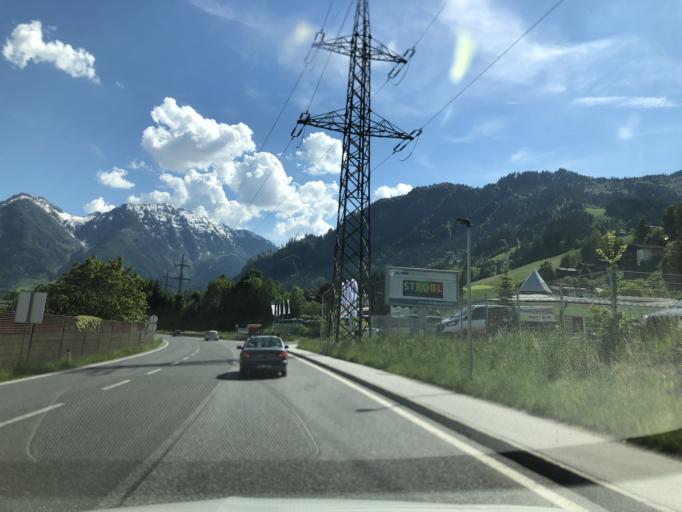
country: AT
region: Salzburg
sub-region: Politischer Bezirk Sankt Johann im Pongau
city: Sankt Johann im Pongau
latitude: 47.3491
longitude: 13.1878
